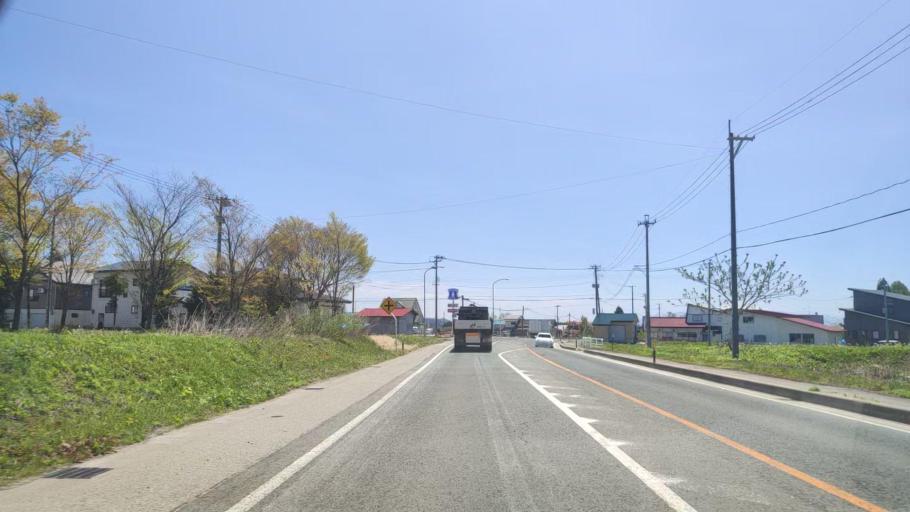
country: JP
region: Yamagata
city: Shinjo
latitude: 38.8212
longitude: 140.3264
